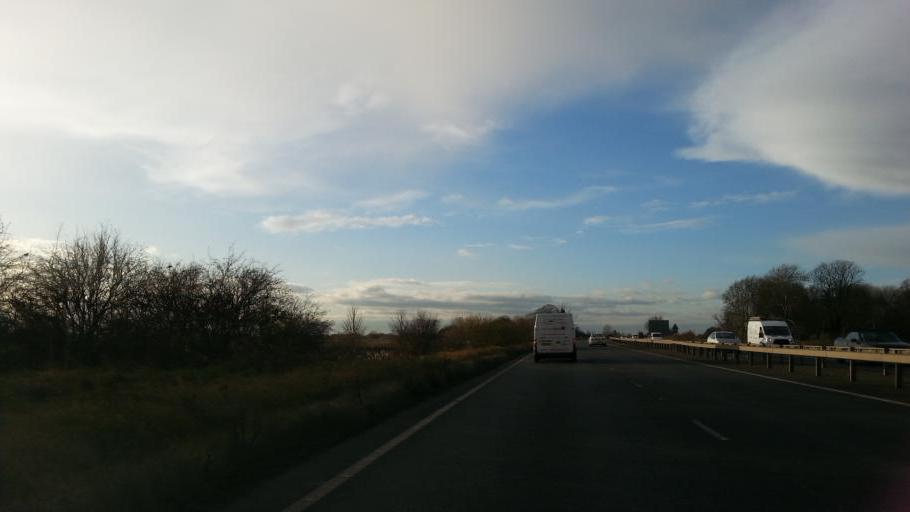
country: GB
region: England
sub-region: Peterborough
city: Thorney
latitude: 52.6217
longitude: -0.0599
